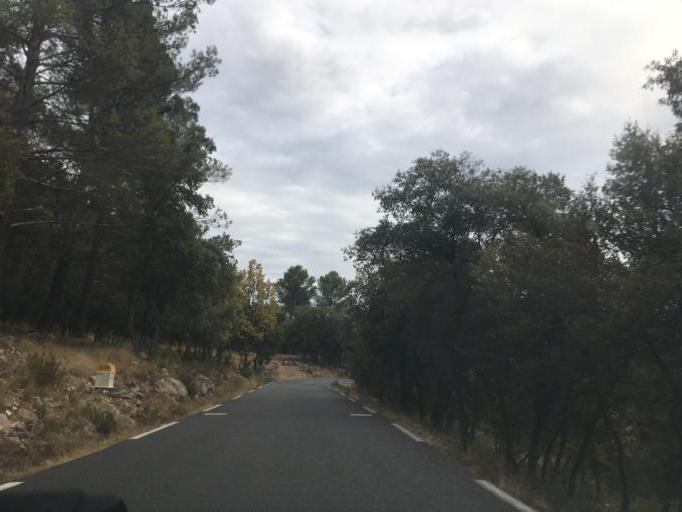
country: FR
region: Provence-Alpes-Cote d'Azur
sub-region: Departement du Var
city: Villecroze
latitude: 43.5660
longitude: 6.3295
